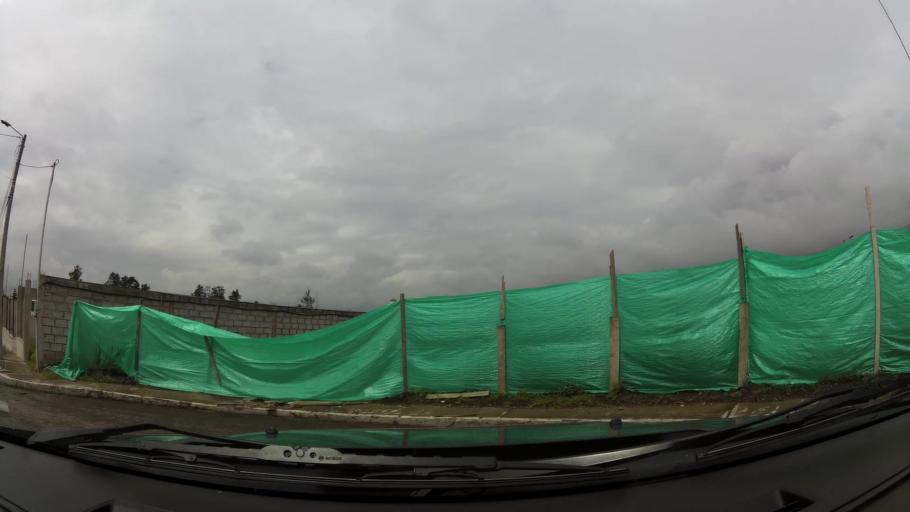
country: EC
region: Pichincha
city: Sangolqui
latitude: -0.3032
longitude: -78.4804
